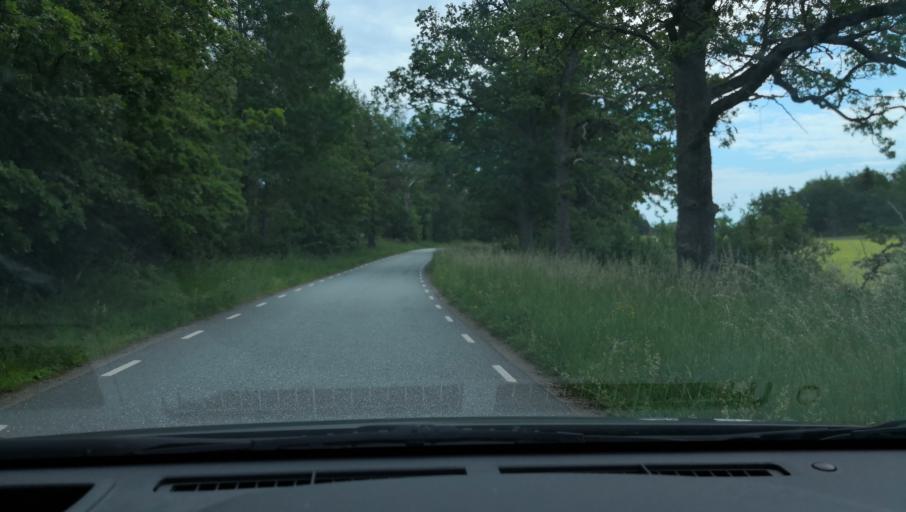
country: SE
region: Uppsala
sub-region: Enkopings Kommun
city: Orsundsbro
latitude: 59.7019
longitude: 17.4263
